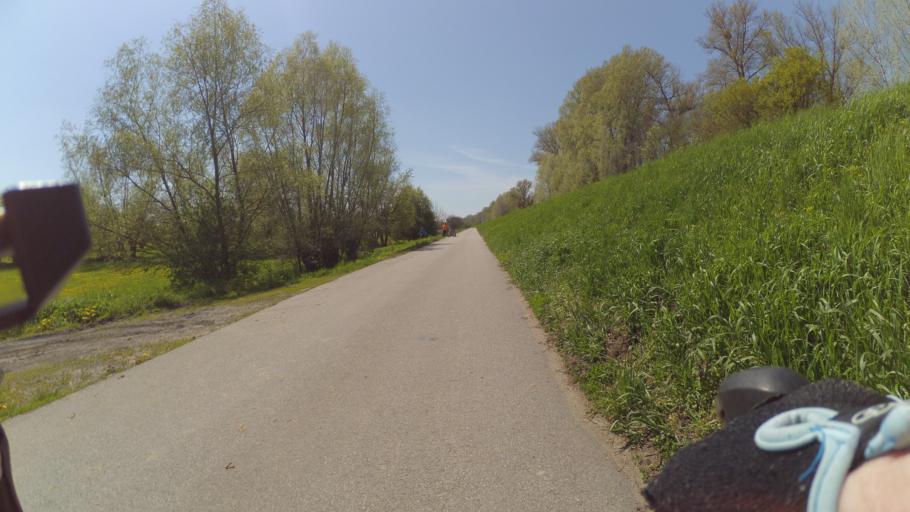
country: PL
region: Masovian Voivodeship
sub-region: Powiat plonski
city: Zaluski
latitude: 52.4016
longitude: 20.4611
